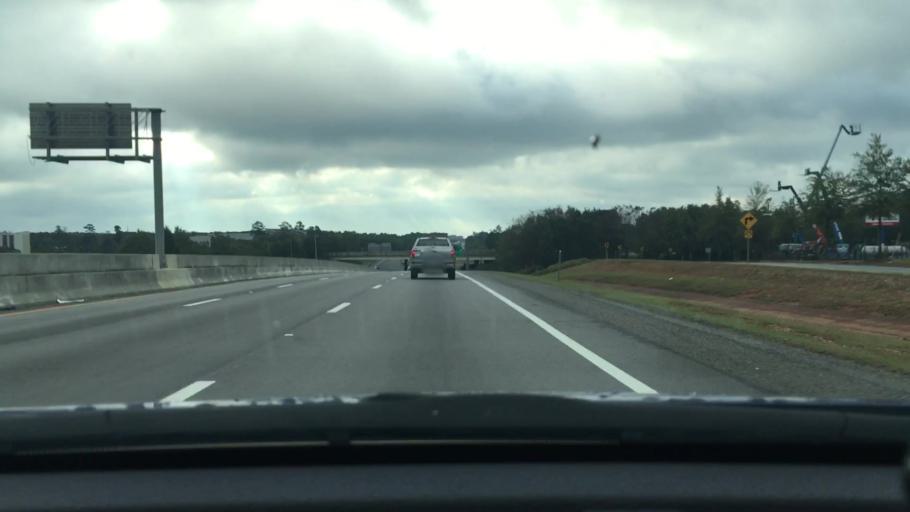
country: US
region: South Carolina
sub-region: Lexington County
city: Irmo
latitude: 34.0929
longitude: -81.1680
